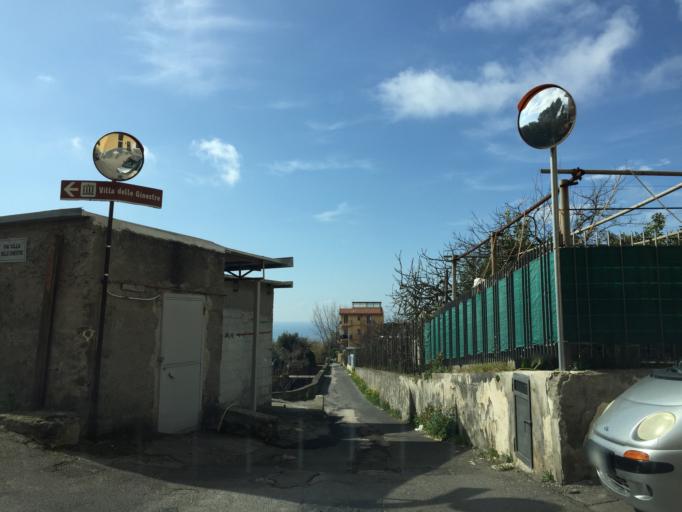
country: IT
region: Campania
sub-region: Provincia di Napoli
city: Torre del Greco
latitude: 40.7781
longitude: 14.4138
